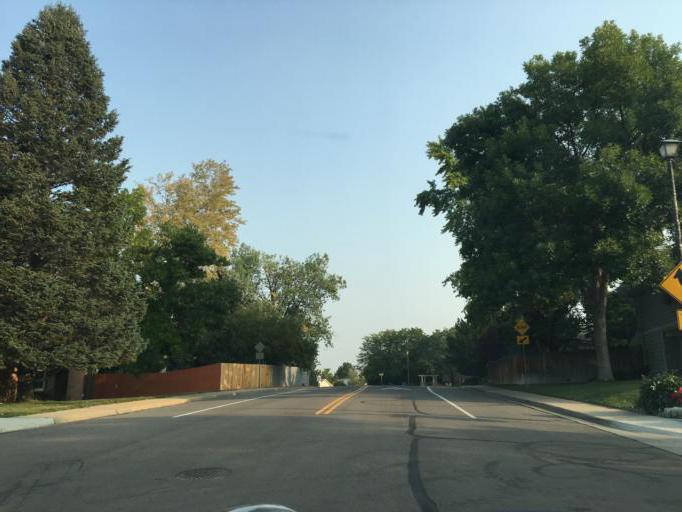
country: US
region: Colorado
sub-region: Adams County
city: Westminster
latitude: 39.8825
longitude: -105.0480
